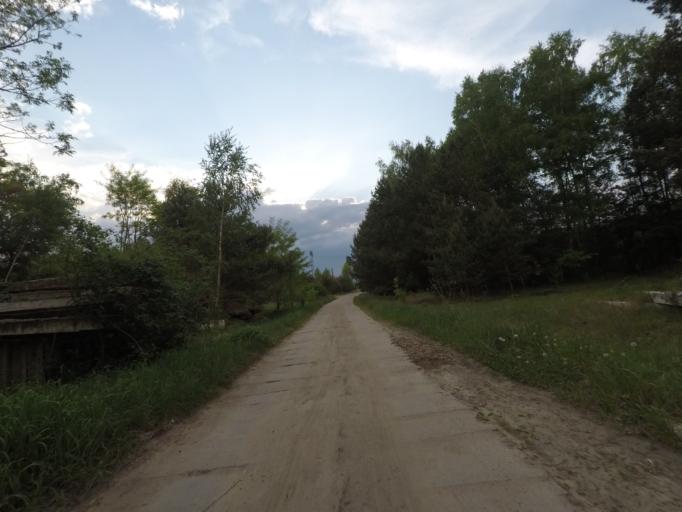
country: DE
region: Brandenburg
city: Eberswalde
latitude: 52.8445
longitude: 13.7518
